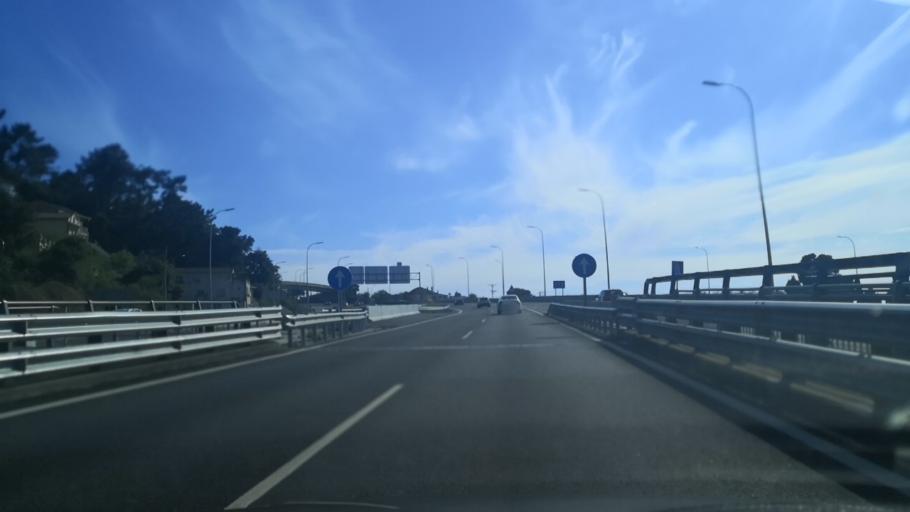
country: ES
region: Galicia
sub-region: Provincia de Pontevedra
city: Redondela
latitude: 42.2792
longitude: -8.6636
